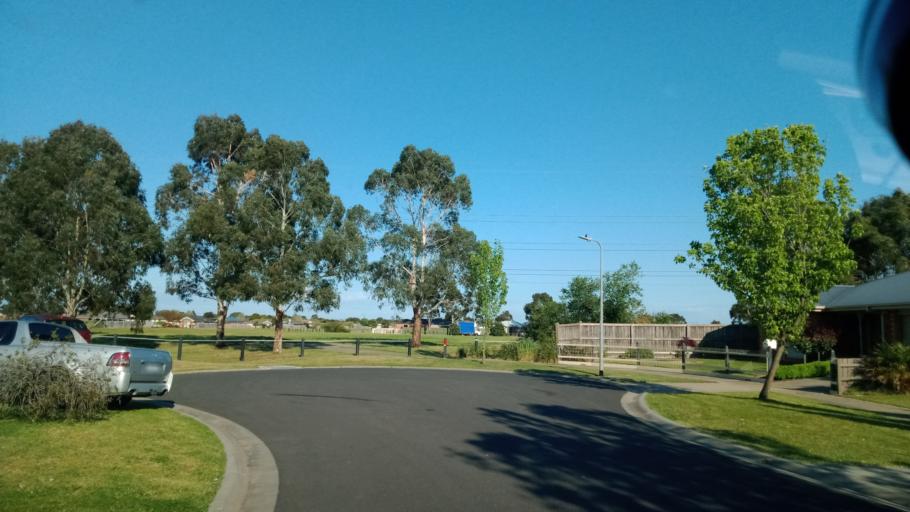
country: AU
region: Victoria
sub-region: Casey
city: Cranbourne West
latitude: -38.0919
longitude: 145.2671
